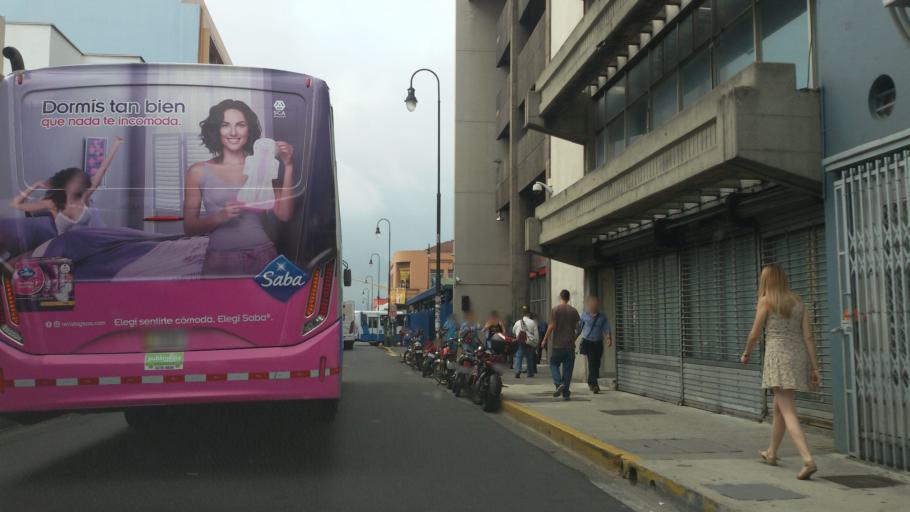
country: CR
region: San Jose
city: San Jose
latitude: 9.9355
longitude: -84.0796
